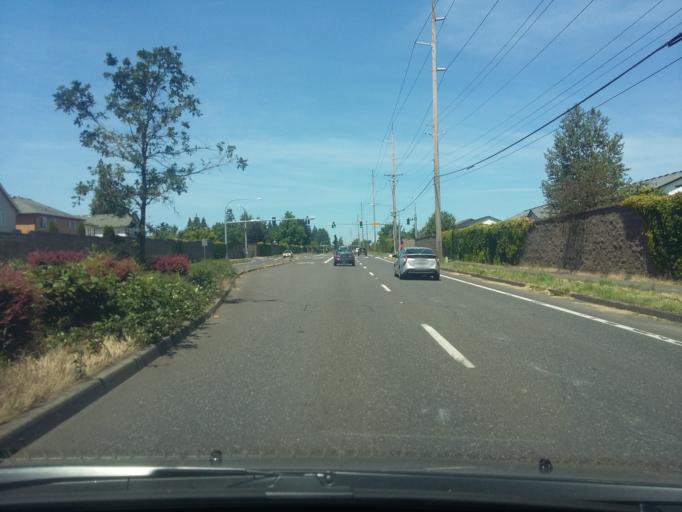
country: US
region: Washington
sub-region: Clark County
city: Mill Plain
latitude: 45.6746
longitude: -122.5059
